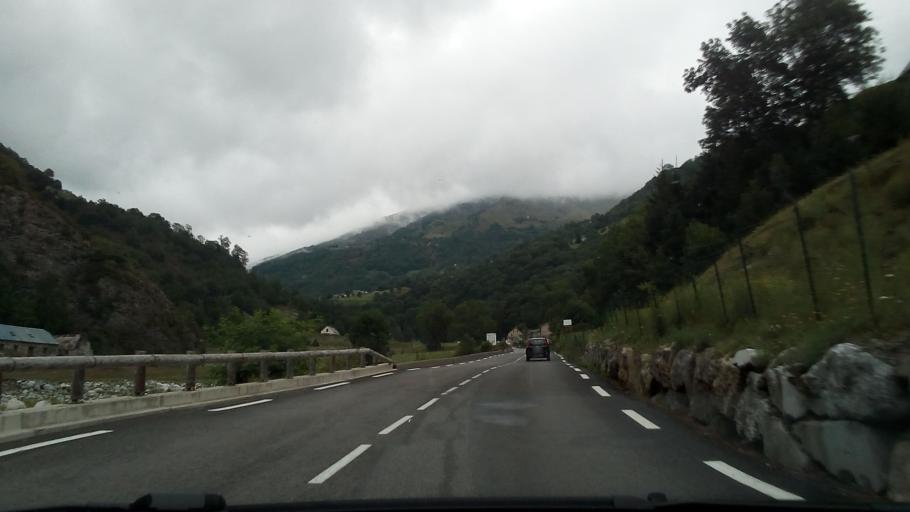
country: FR
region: Midi-Pyrenees
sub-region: Departement des Hautes-Pyrenees
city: Luz-Saint-Sauveur
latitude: 42.8781
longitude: 0.0133
